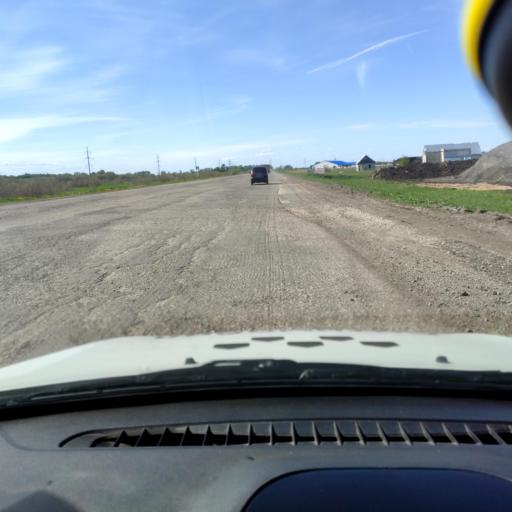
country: RU
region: Samara
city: Tol'yatti
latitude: 53.6644
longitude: 49.4215
